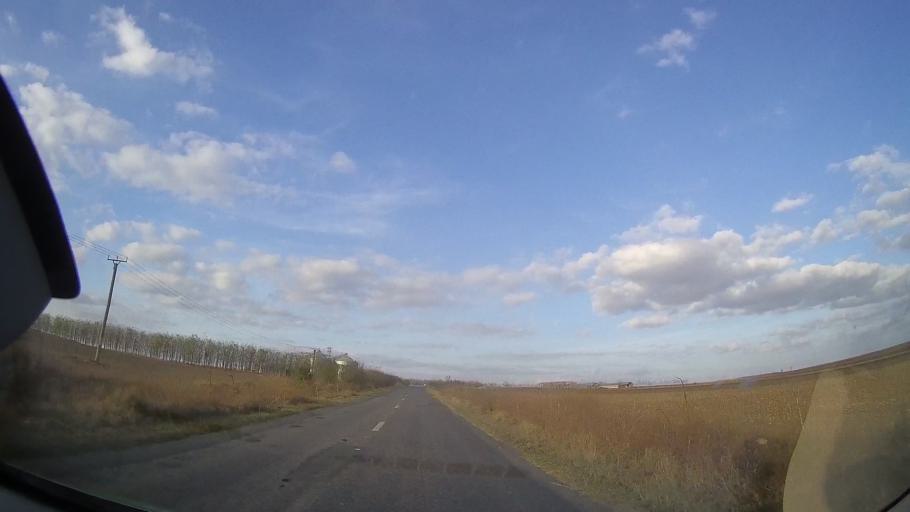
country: RO
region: Constanta
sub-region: Comuna Dumbraveni
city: Dumbraveni
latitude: 43.9238
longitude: 28.0296
